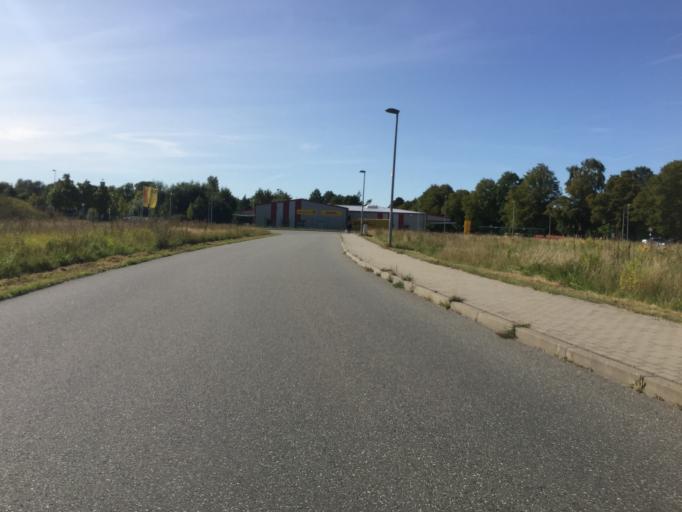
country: DE
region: Schleswig-Holstein
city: Itzehoe
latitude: 53.9128
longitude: 9.5088
